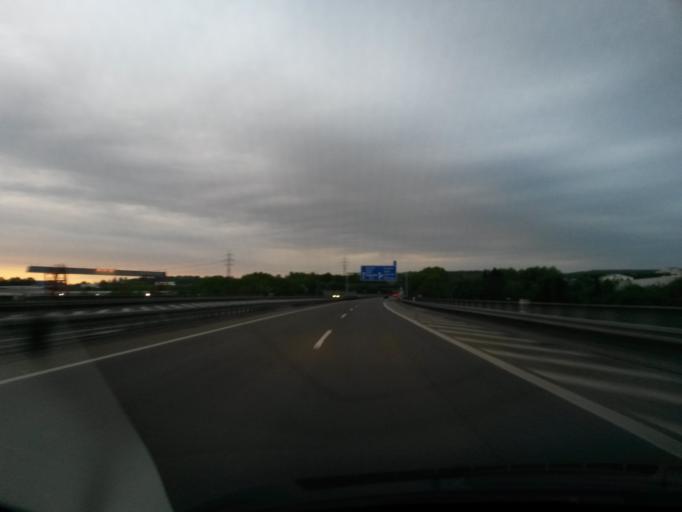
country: DE
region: Hesse
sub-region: Regierungsbezirk Kassel
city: Eichenzell
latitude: 50.4835
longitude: 9.7127
